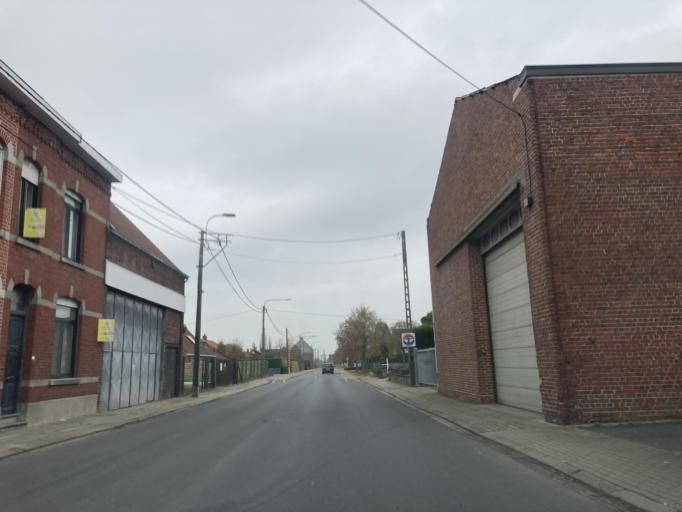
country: BE
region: Flanders
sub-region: Provincie West-Vlaanderen
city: Lendelede
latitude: 50.8708
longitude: 3.2419
